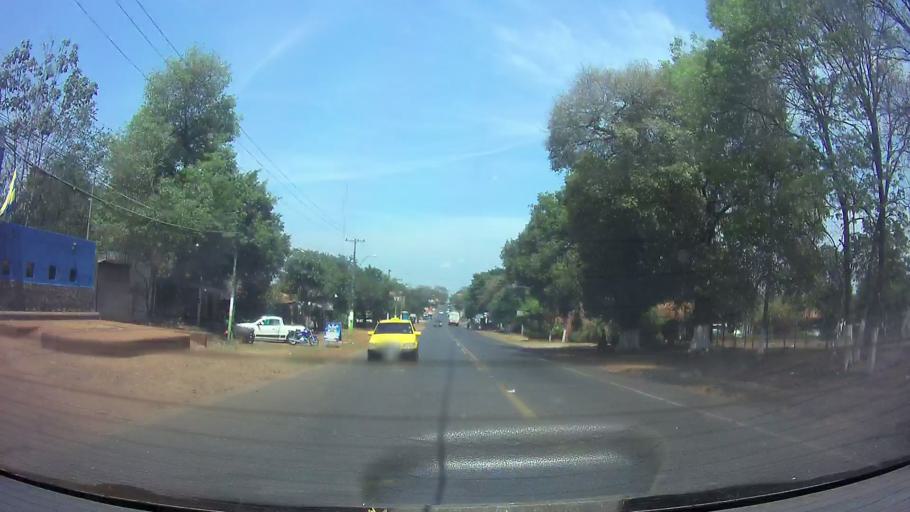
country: PY
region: Central
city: Guarambare
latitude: -25.4401
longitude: -57.4436
